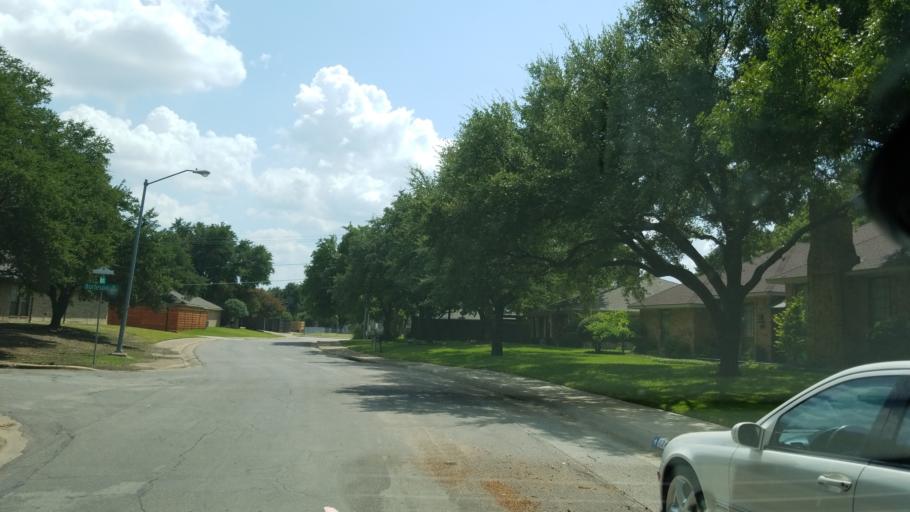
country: US
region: Texas
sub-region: Dallas County
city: Richardson
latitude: 32.9174
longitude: -96.7218
